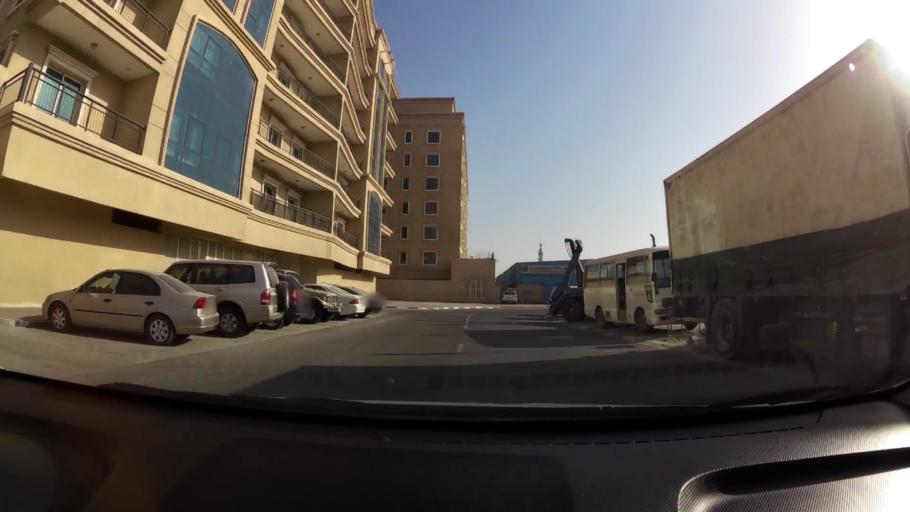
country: AE
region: Ash Shariqah
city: Sharjah
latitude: 25.2865
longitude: 55.3896
